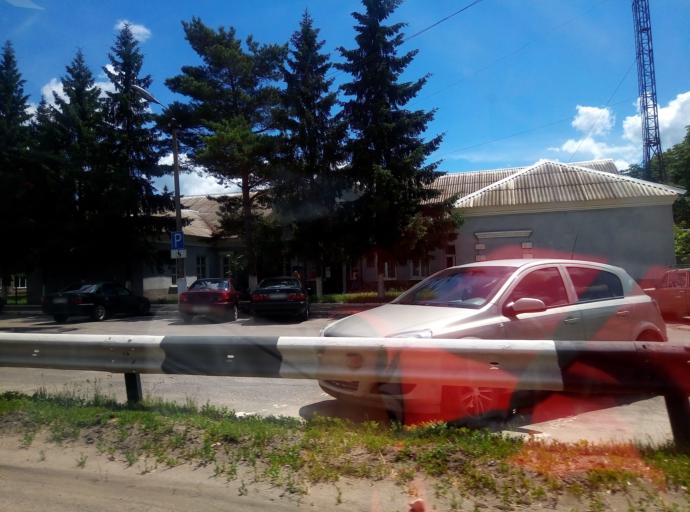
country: RU
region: Kursk
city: Oboyan'
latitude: 51.2151
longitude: 36.2930
